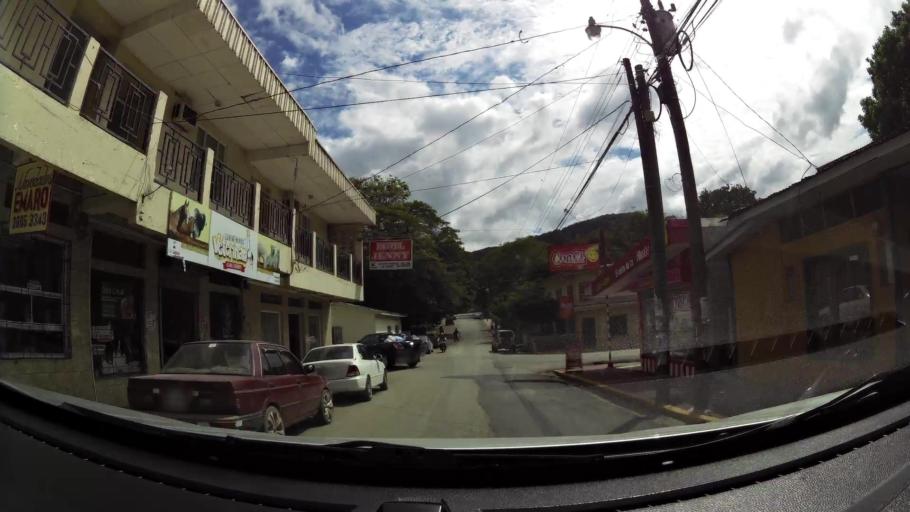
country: CR
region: Guanacaste
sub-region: Canton de Nicoya
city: Nicoya
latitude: 10.1417
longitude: -85.4527
